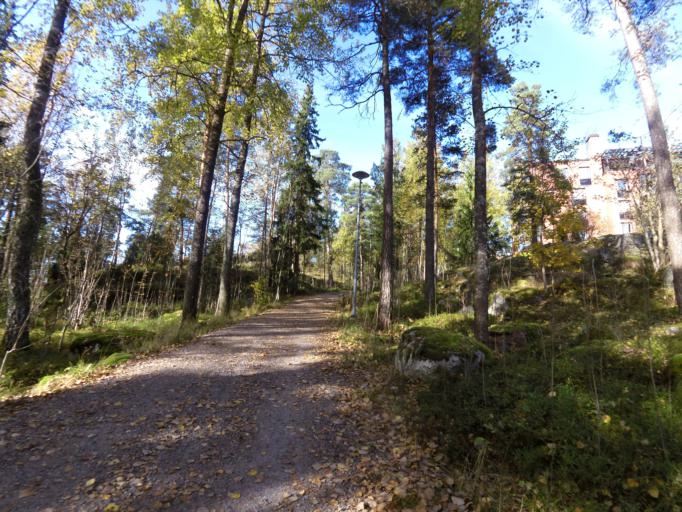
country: FI
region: Uusimaa
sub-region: Helsinki
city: Espoo
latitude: 60.1471
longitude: 24.6375
